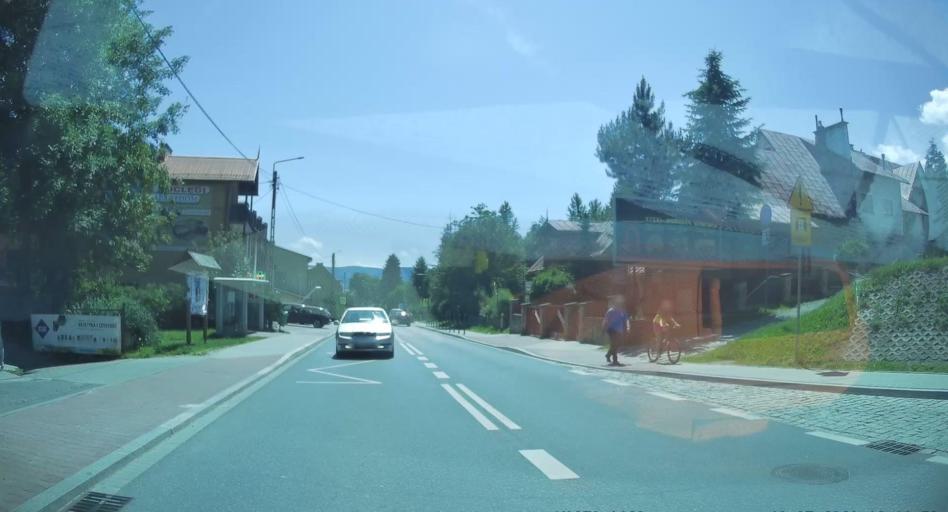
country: PL
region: Lesser Poland Voivodeship
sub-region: Powiat nowosadecki
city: Krynica-Zdroj
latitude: 49.4059
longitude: 20.9533
